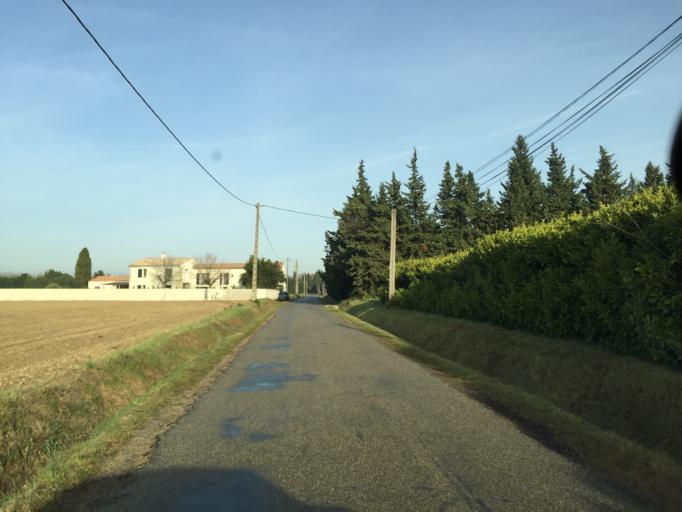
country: FR
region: Provence-Alpes-Cote d'Azur
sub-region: Departement du Vaucluse
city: Orange
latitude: 44.1439
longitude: 4.7871
